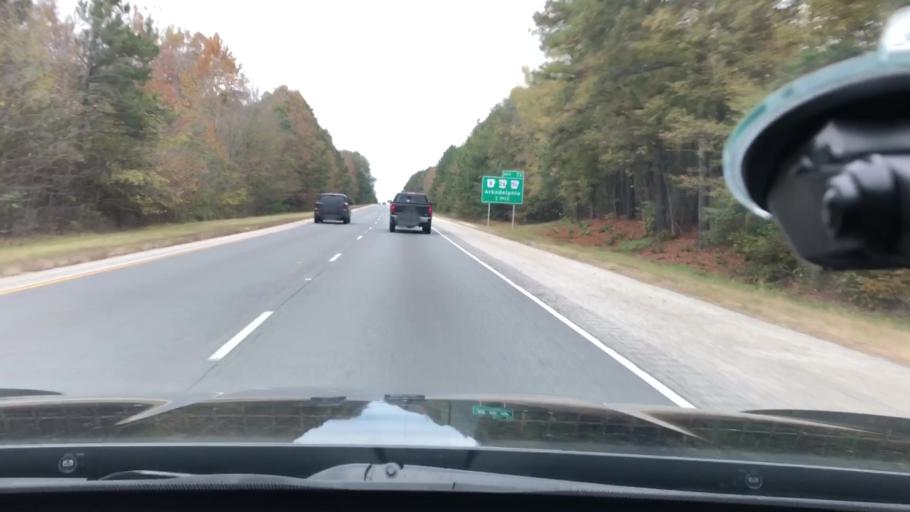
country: US
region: Arkansas
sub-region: Clark County
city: Arkadelphia
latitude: 34.1008
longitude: -93.1023
